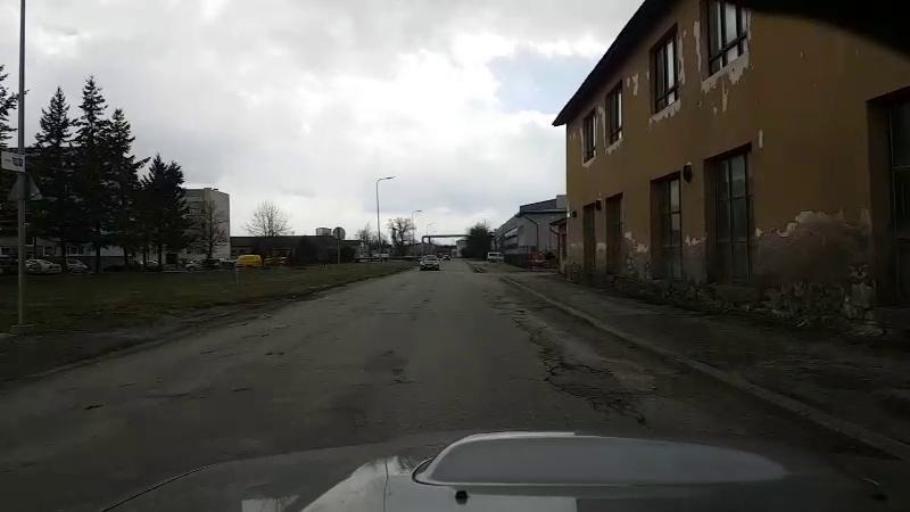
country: EE
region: Jaervamaa
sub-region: Paide linn
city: Paide
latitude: 58.8846
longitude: 25.5600
